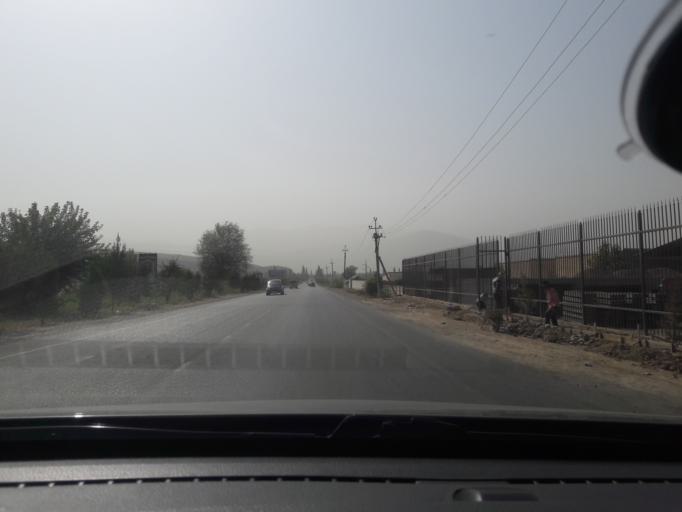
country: TJ
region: Republican Subordination
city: Vahdat
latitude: 38.5308
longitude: 69.0258
